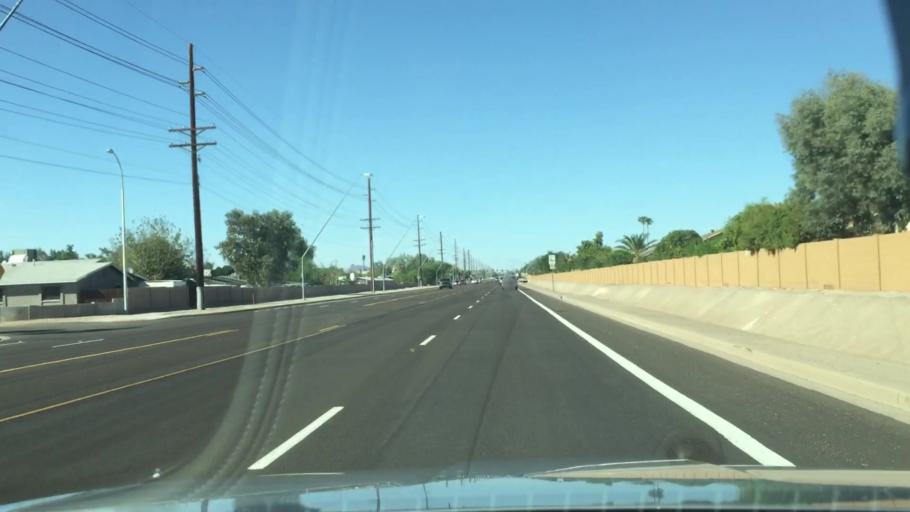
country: US
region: Arizona
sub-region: Pinal County
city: Apache Junction
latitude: 33.4072
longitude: -111.6601
